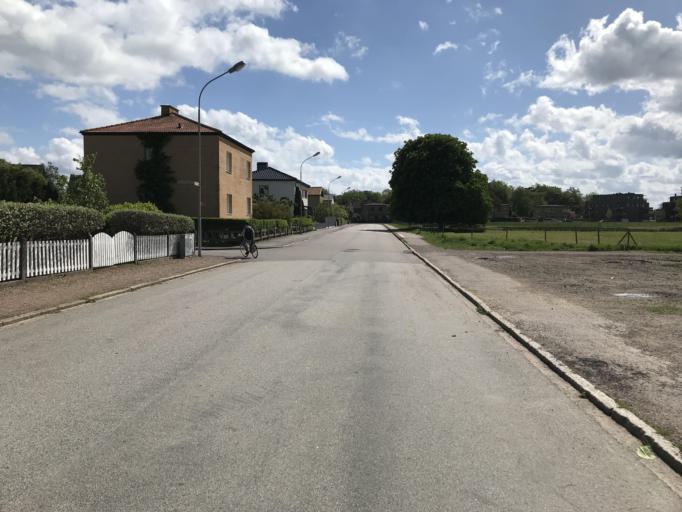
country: SE
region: Skane
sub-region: Landskrona
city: Landskrona
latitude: 55.8812
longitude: 12.8215
